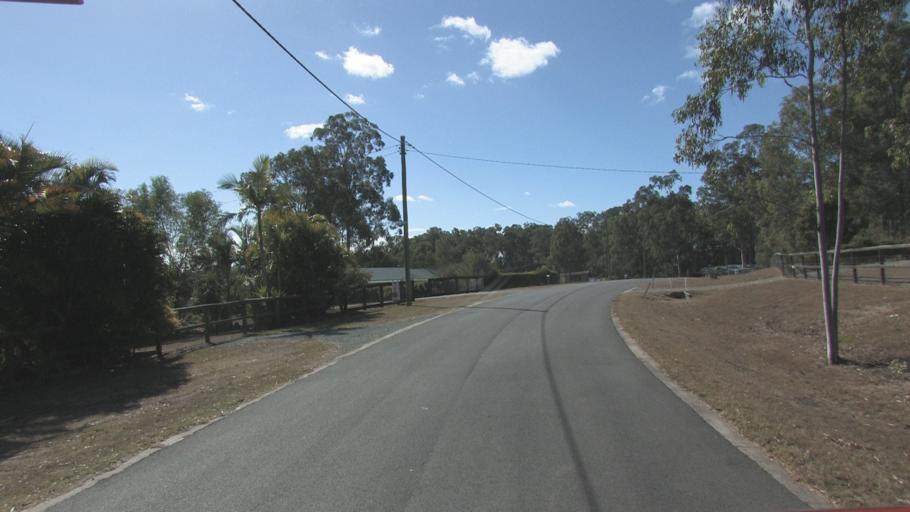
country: AU
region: Queensland
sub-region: Logan
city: Cedar Vale
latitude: -27.8785
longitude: 153.0068
